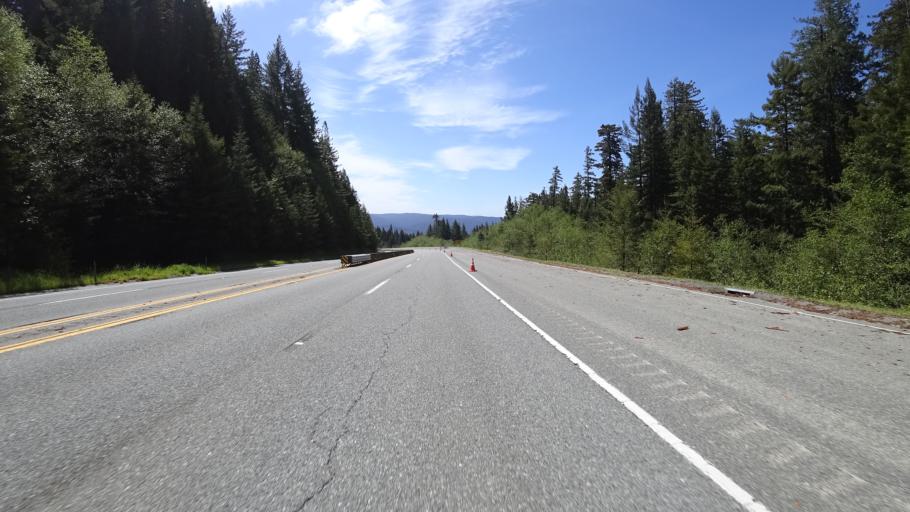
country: US
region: California
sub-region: Humboldt County
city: Westhaven-Moonstone
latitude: 41.3794
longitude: -123.9949
